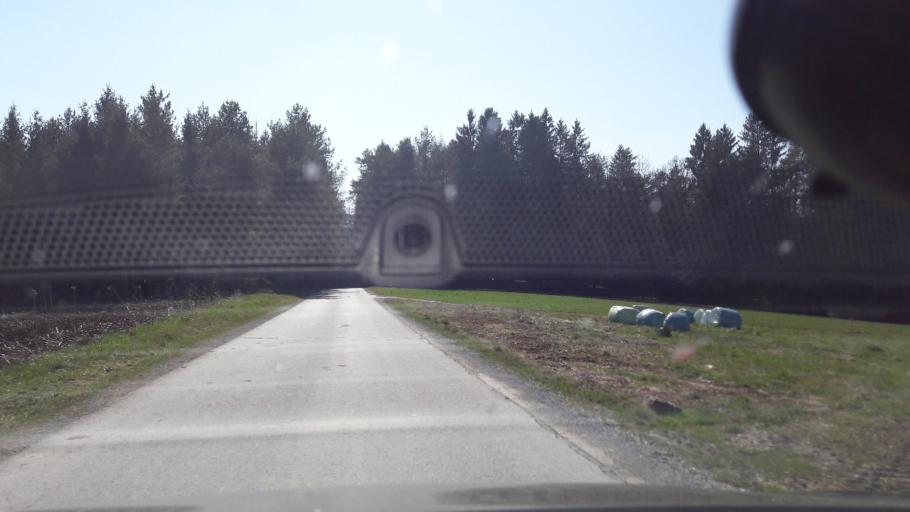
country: AT
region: Styria
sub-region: Politischer Bezirk Graz-Umgebung
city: Hitzendorf
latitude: 47.0324
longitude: 15.3136
